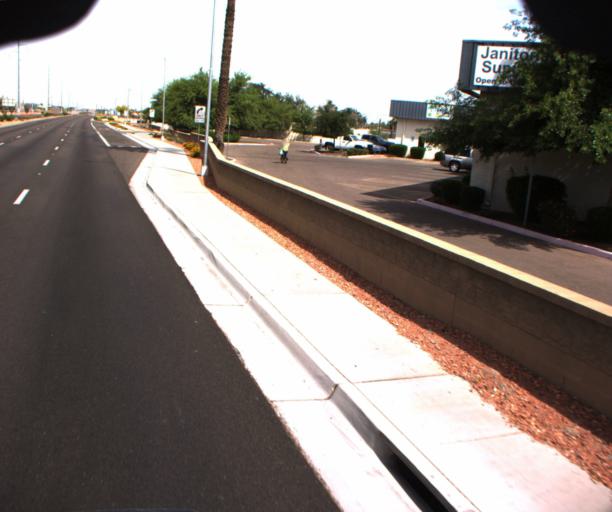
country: US
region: Arizona
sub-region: Maricopa County
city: Glendale
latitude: 33.5431
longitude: -112.1912
